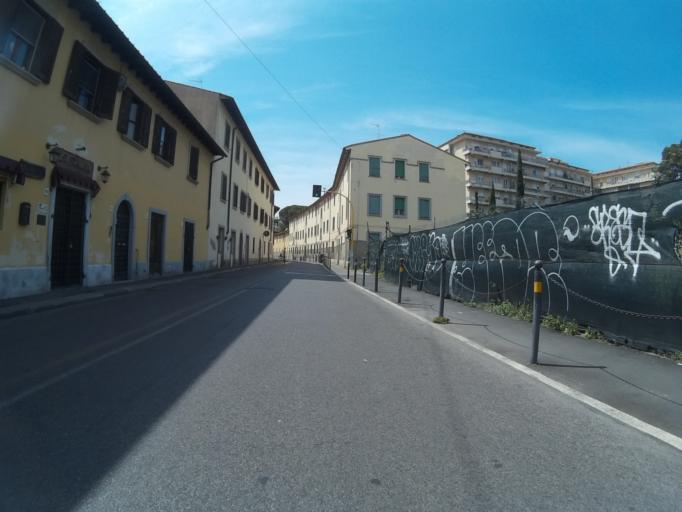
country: IT
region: Tuscany
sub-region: Provincia di Livorno
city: Livorno
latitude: 43.5370
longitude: 10.3136
